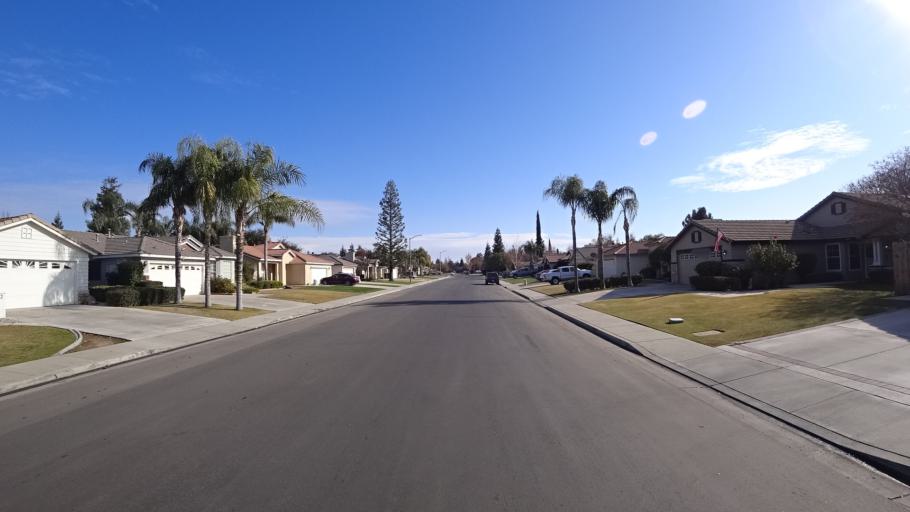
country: US
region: California
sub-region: Kern County
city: Greenacres
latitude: 35.4130
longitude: -119.0977
